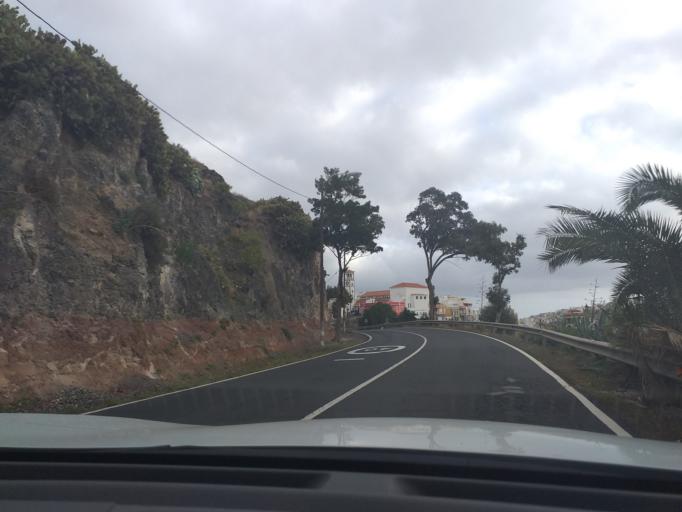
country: ES
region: Canary Islands
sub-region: Provincia de Las Palmas
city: Arucas
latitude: 28.1153
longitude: -15.4922
